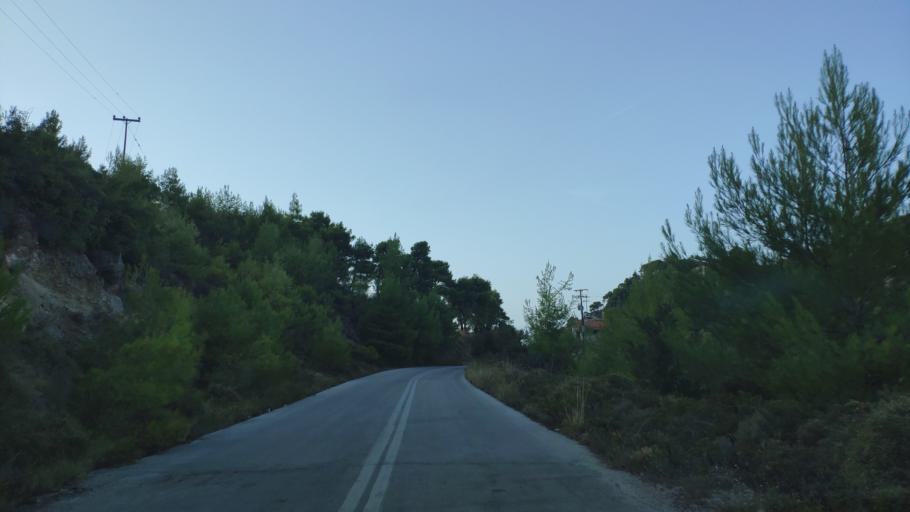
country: GR
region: West Greece
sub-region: Nomos Achaias
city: Aiyira
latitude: 38.0972
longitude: 22.4083
